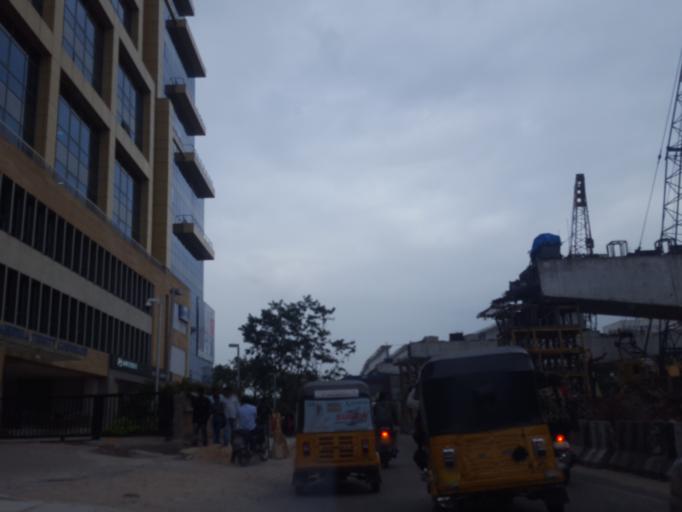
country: IN
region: Telangana
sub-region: Rangareddi
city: Kukatpalli
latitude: 17.4897
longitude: 78.3924
